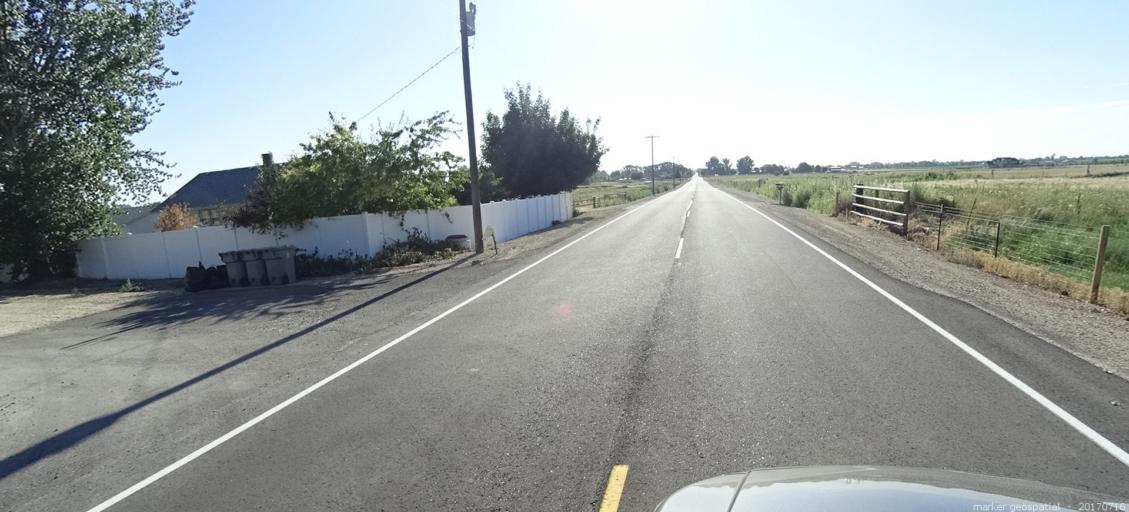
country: US
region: Idaho
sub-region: Ada County
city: Kuna
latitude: 43.5467
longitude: -116.4793
